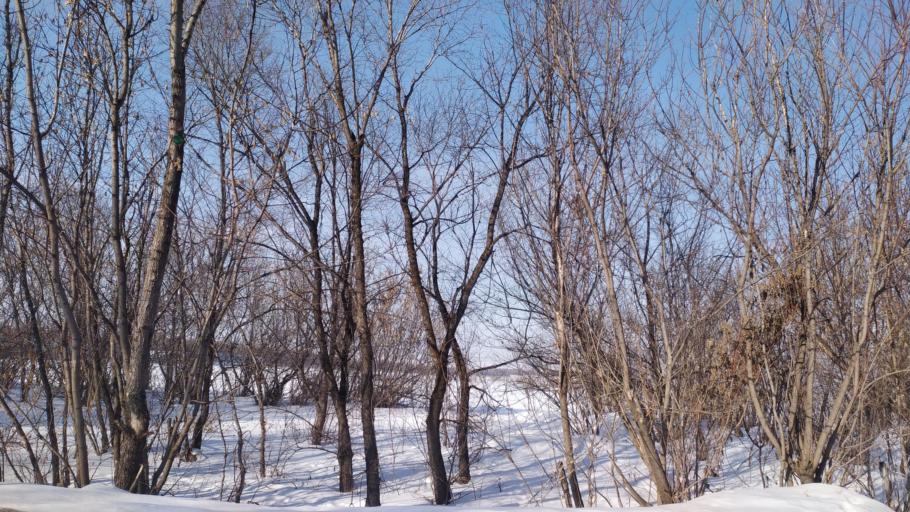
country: KZ
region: Almaty Oblysy
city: Burunday
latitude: 43.2417
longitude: 76.4270
